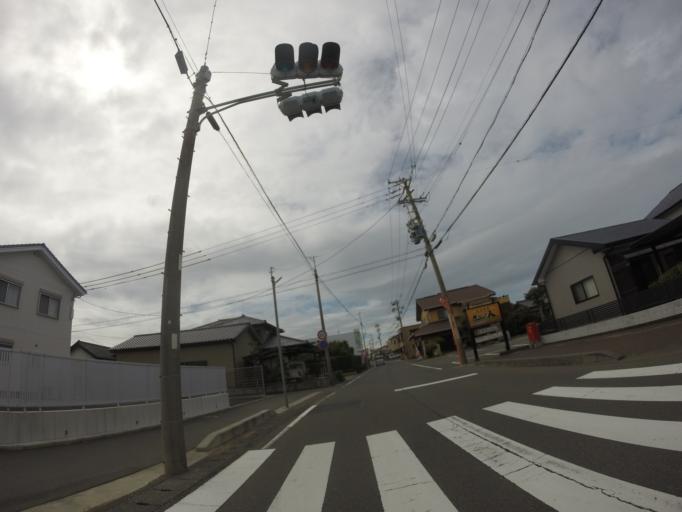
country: JP
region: Shizuoka
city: Oyama
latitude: 34.6048
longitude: 138.2143
